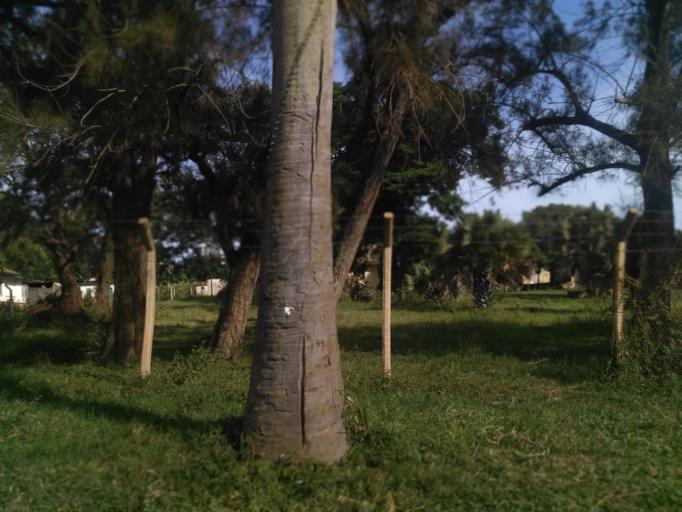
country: UG
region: Eastern Region
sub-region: Jinja District
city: Jinja
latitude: 0.4206
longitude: 33.1994
